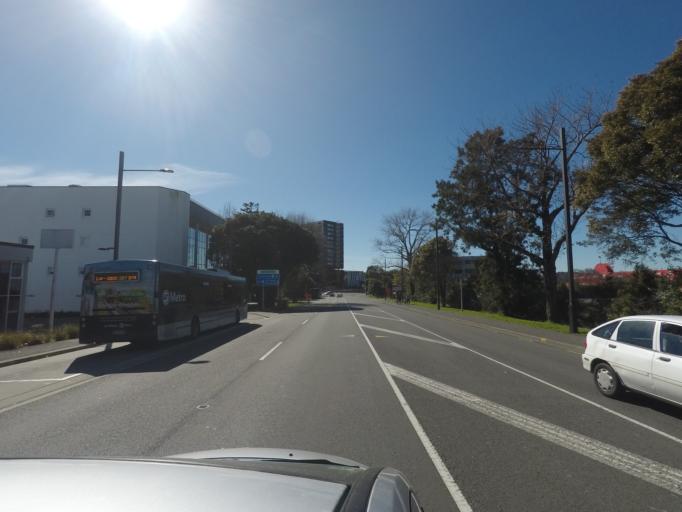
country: NZ
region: Auckland
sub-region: Auckland
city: Waitakere
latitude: -36.9113
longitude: 174.6826
